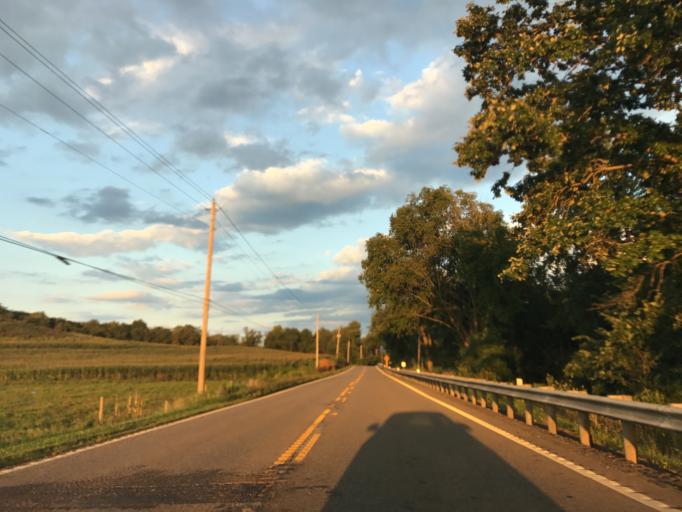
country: US
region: Ohio
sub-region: Stark County
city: Minerva
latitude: 40.7423
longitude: -81.0177
